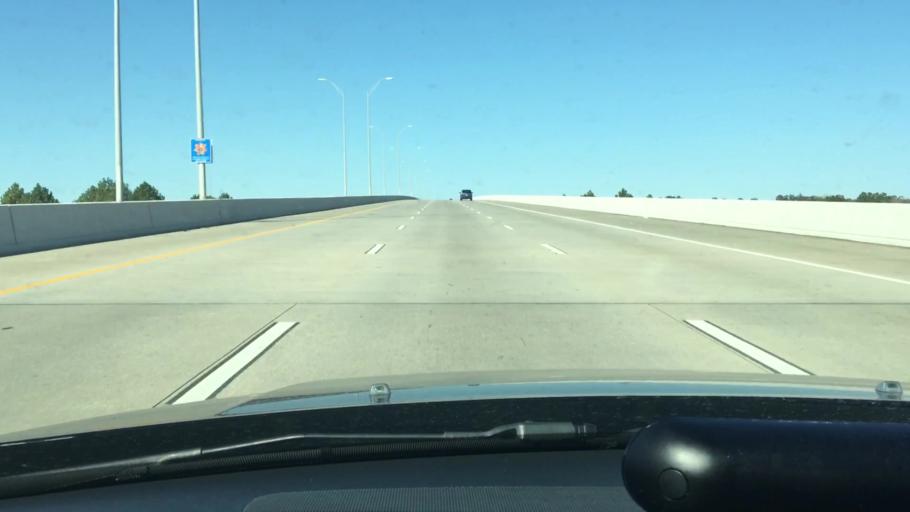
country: US
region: Texas
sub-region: Harris County
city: Cloverleaf
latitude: 29.8295
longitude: -95.1728
